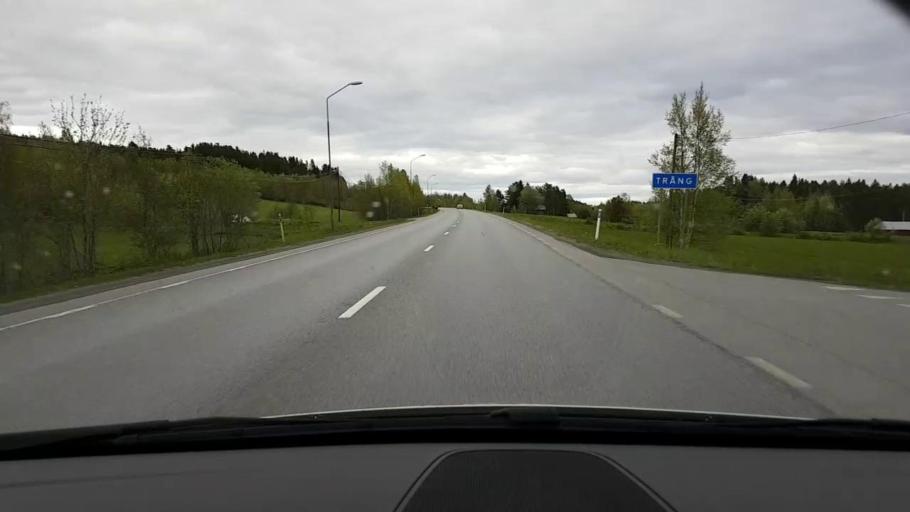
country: SE
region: Jaemtland
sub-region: Krokoms Kommun
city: Valla
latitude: 63.3212
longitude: 14.0641
